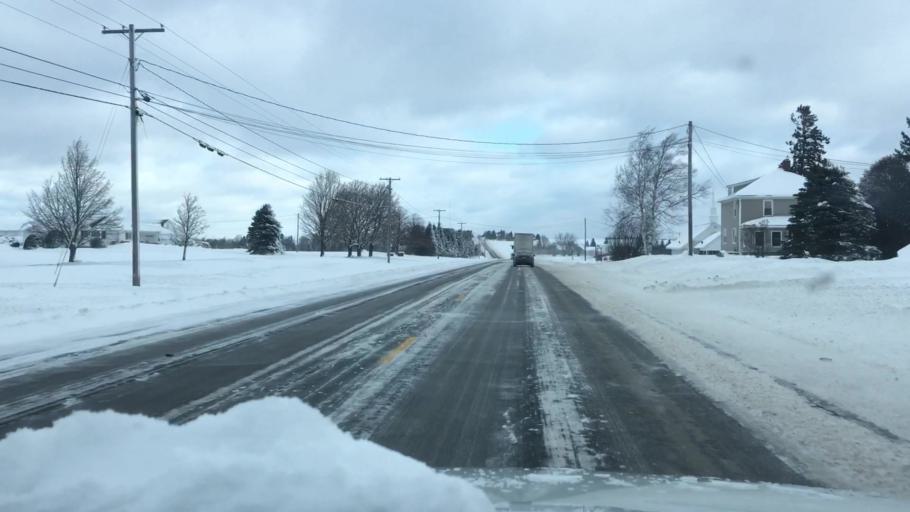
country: US
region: Maine
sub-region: Aroostook County
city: Presque Isle
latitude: 46.7409
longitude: -67.9971
